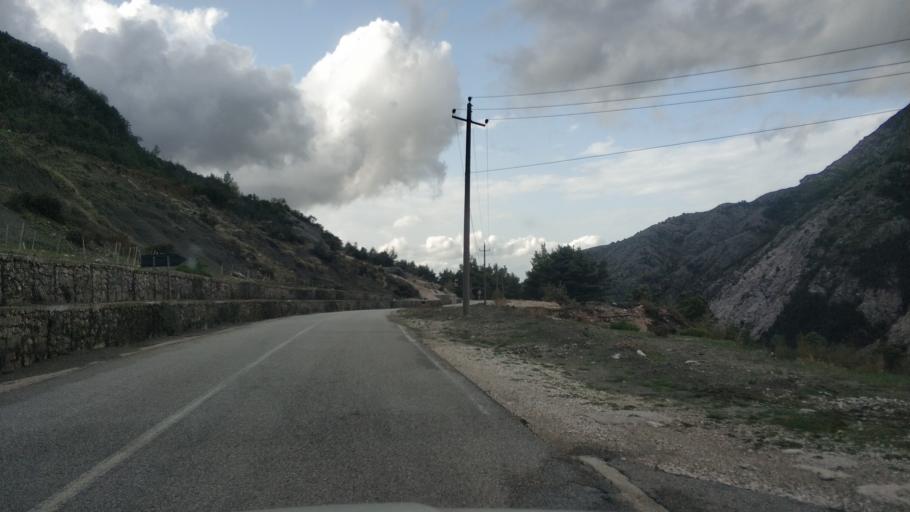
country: AL
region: Vlore
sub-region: Rrethi i Vlores
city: Orikum
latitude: 40.2472
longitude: 19.5462
